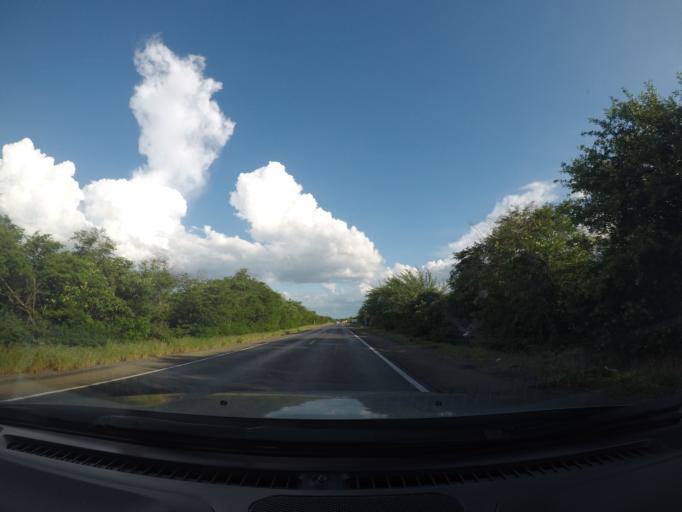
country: BR
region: Bahia
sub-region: Oliveira Dos Brejinhos
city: Oliveira dos Brejinhos
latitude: -12.0954
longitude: -42.9249
